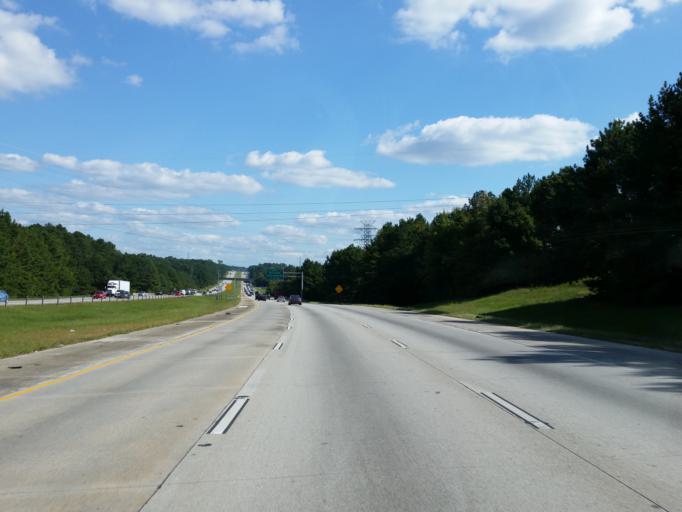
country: US
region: Georgia
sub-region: Clayton County
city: Conley
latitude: 33.6521
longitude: -84.3232
